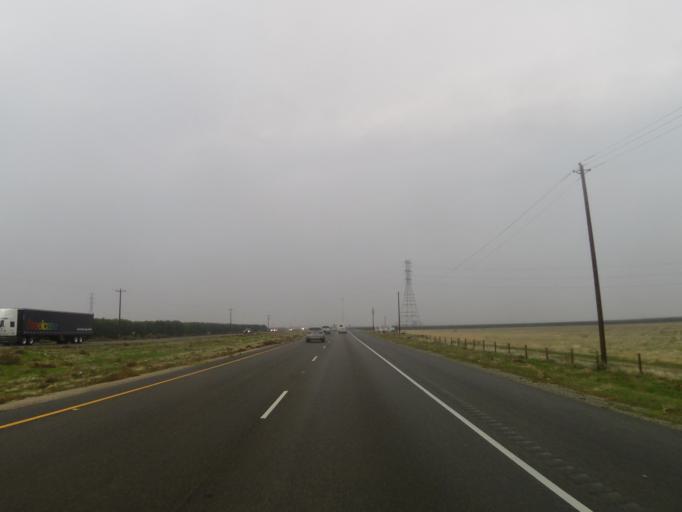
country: US
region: California
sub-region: Kern County
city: Weedpatch
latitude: 35.0461
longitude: -118.9852
